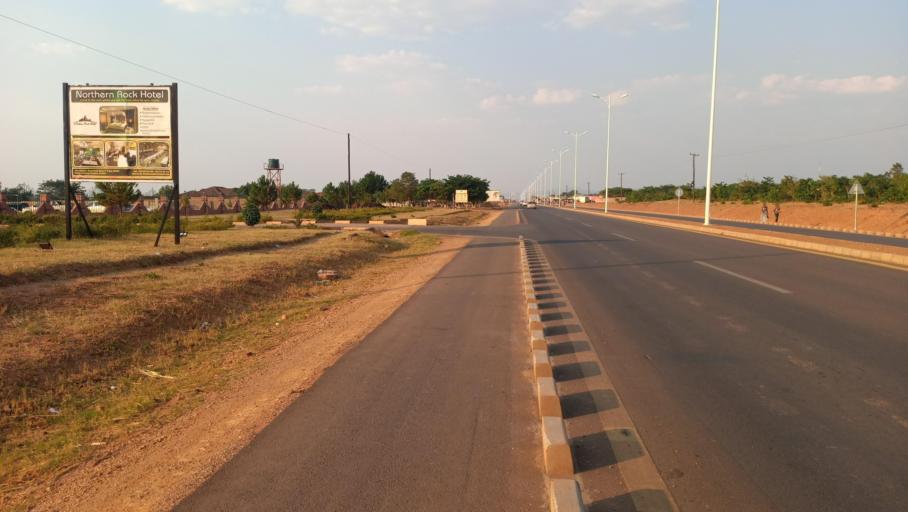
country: ZM
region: Northern
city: Mpika
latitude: -11.8495
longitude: 31.4417
